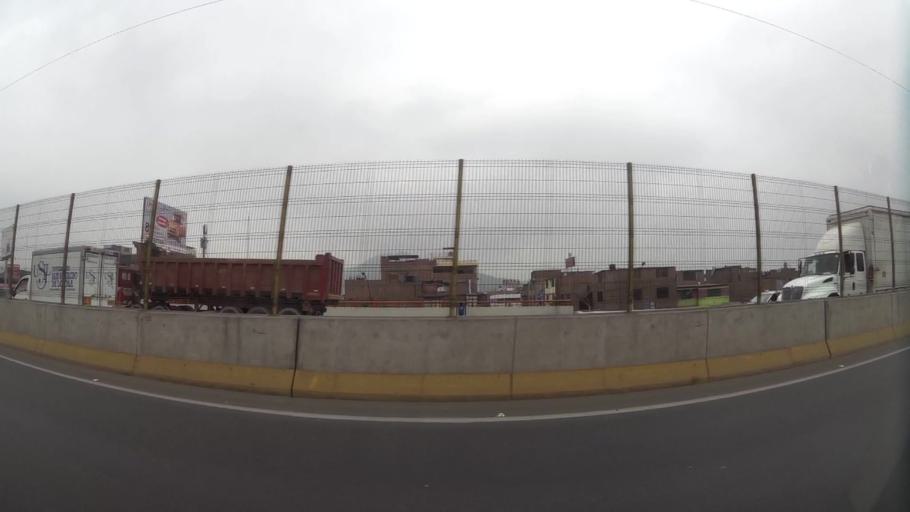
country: PE
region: Lima
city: Lima
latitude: -12.0303
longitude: -77.0011
